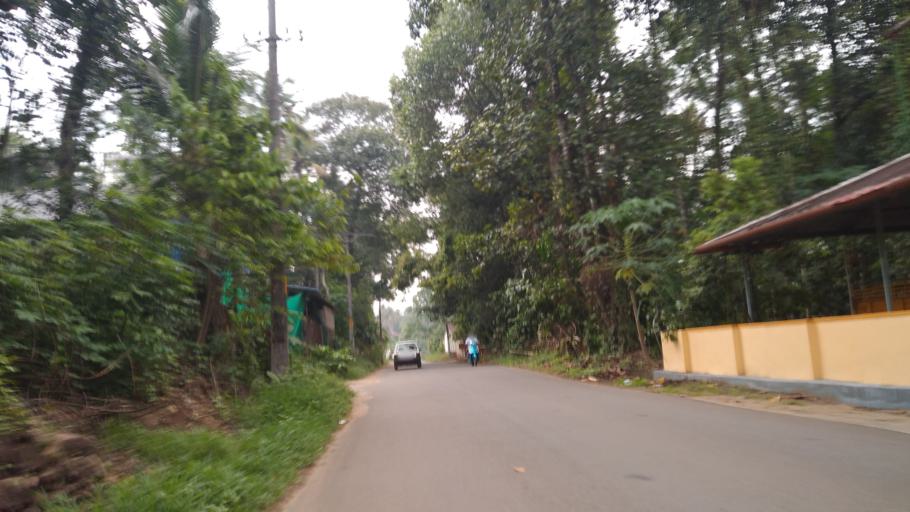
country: IN
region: Kerala
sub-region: Ernakulam
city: Perumbavoor
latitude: 10.0874
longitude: 76.5123
